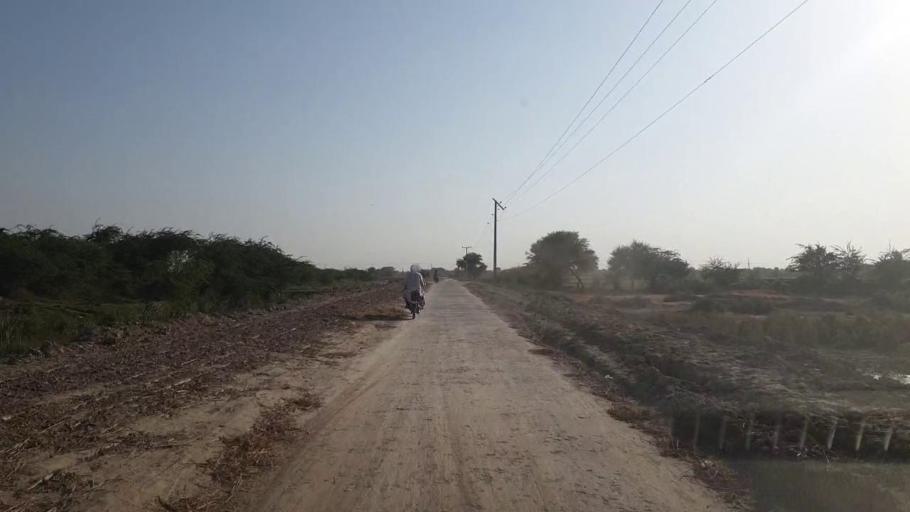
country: PK
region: Sindh
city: Talhar
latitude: 24.9103
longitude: 68.7430
